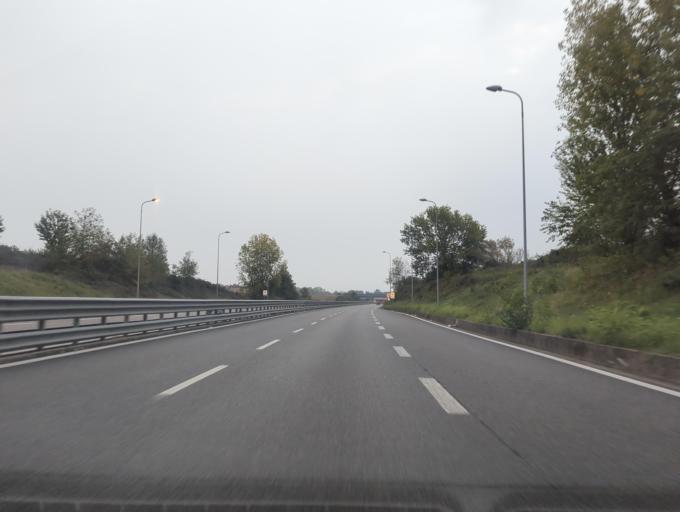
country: IT
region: Piedmont
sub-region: Provincia di Novara
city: Torrion Quartara
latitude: 45.4242
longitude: 8.6263
